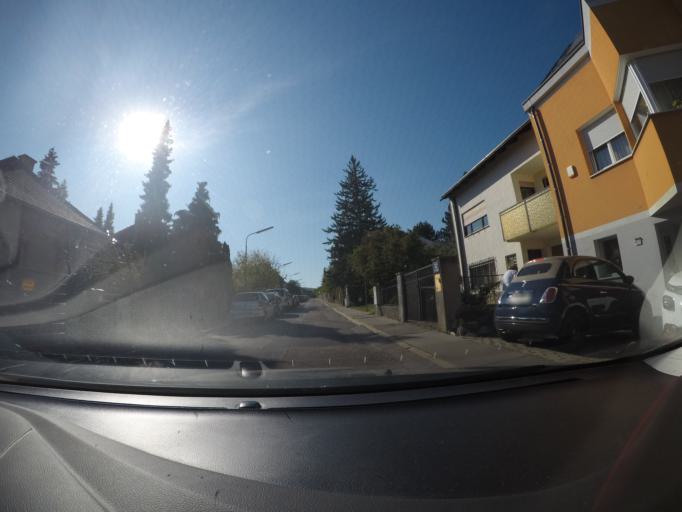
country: AT
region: Lower Austria
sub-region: Politischer Bezirk Modling
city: Perchtoldsdorf
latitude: 48.1679
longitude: 16.2621
